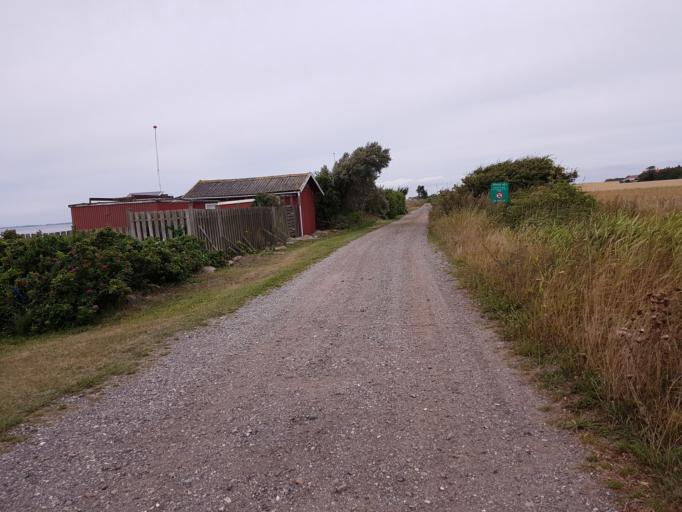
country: DK
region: Zealand
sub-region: Guldborgsund Kommune
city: Nykobing Falster
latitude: 54.5862
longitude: 11.9226
